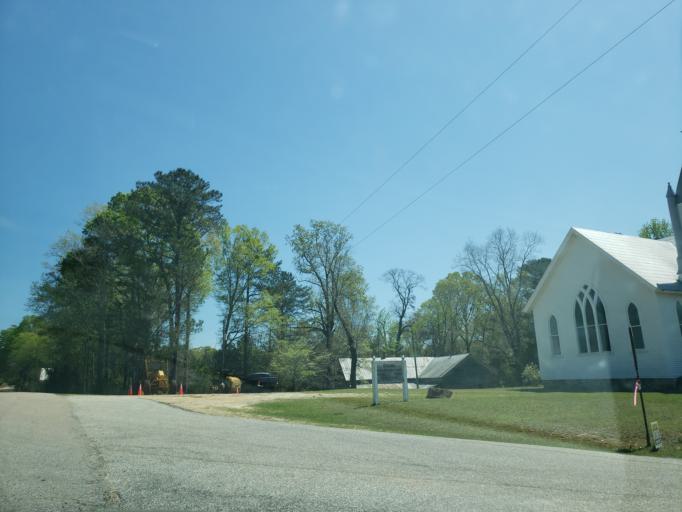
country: US
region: Alabama
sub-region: Tallapoosa County
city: Camp Hill
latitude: 32.6871
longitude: -85.6692
